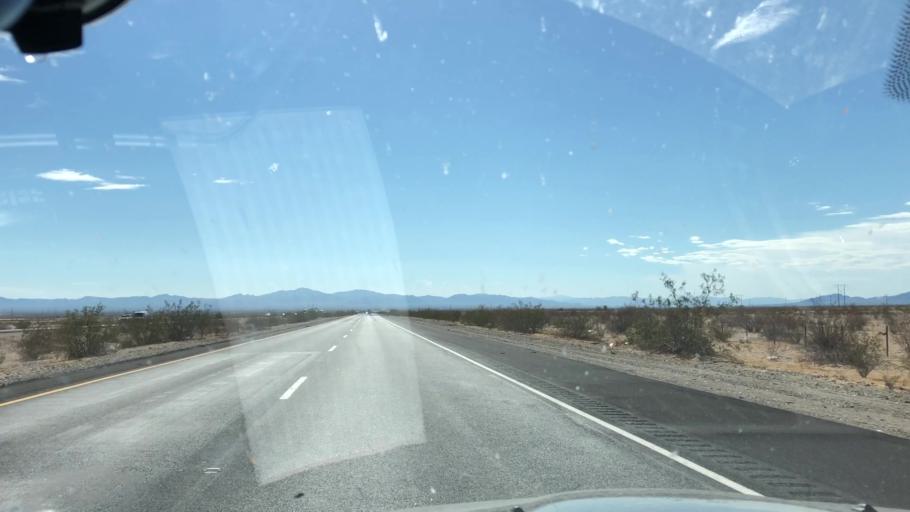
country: US
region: California
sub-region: Riverside County
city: Mesa Verde
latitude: 33.6096
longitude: -114.8536
